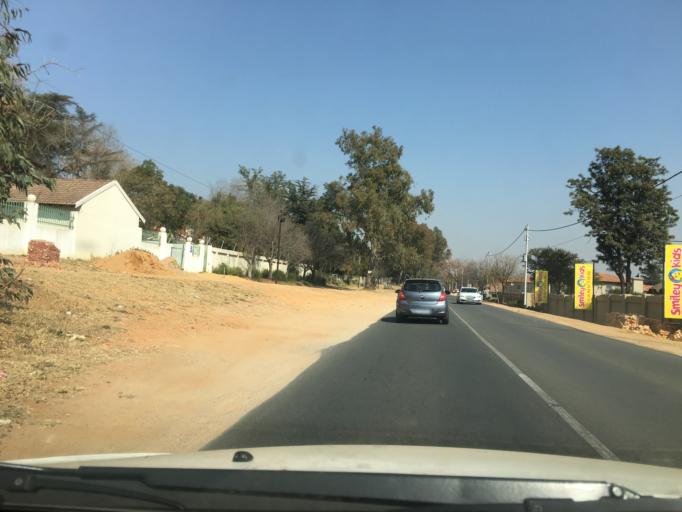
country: ZA
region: Gauteng
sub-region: City of Johannesburg Metropolitan Municipality
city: Midrand
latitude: -26.0608
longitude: 28.0562
